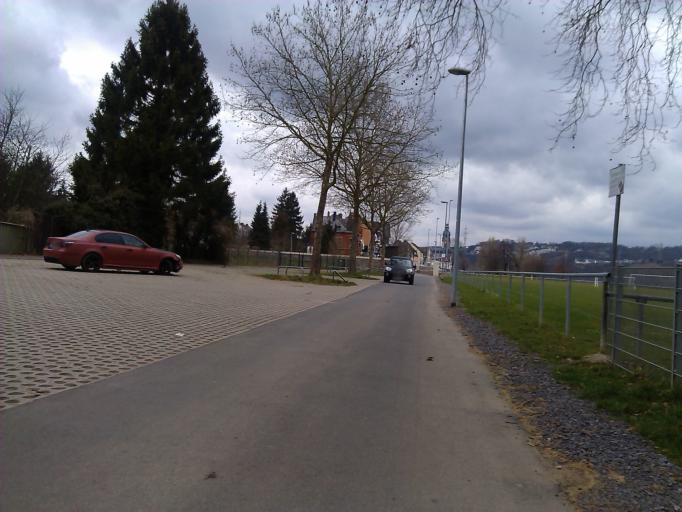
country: DE
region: Rheinland-Pfalz
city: Urbar
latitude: 50.3714
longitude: 7.6082
